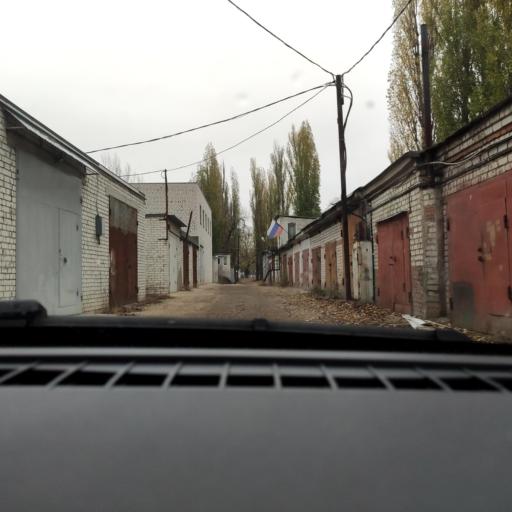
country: RU
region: Voronezj
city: Maslovka
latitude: 51.6096
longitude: 39.2428
